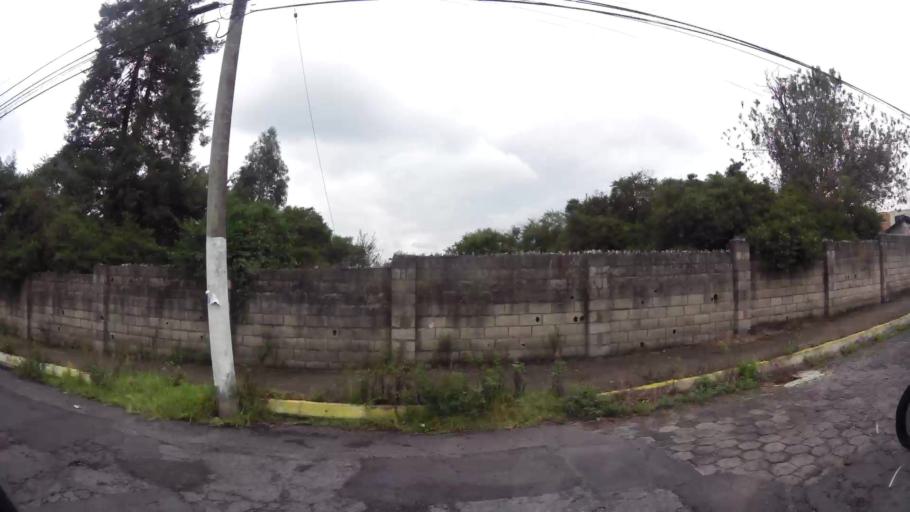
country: EC
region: Pichincha
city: Sangolqui
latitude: -0.3024
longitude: -78.4704
